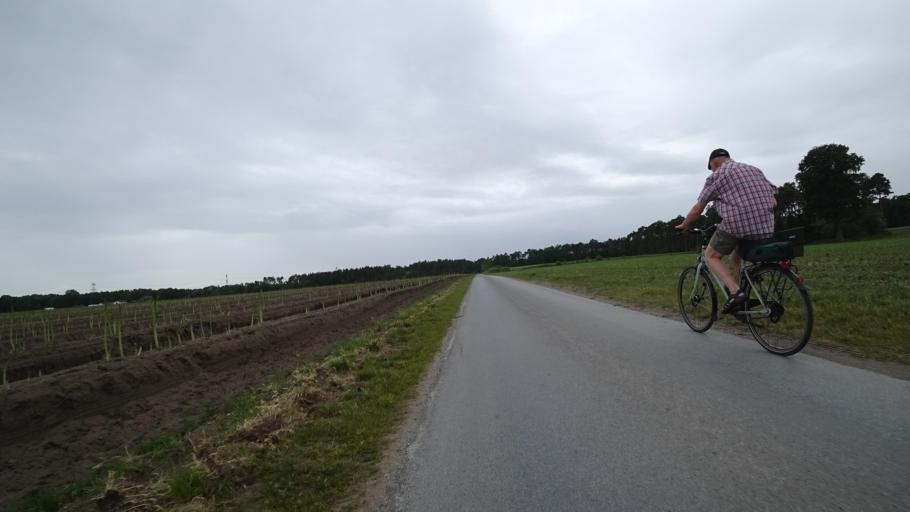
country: DE
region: North Rhine-Westphalia
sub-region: Regierungsbezirk Detmold
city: Rheda-Wiedenbruck
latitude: 51.9134
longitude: 8.2971
